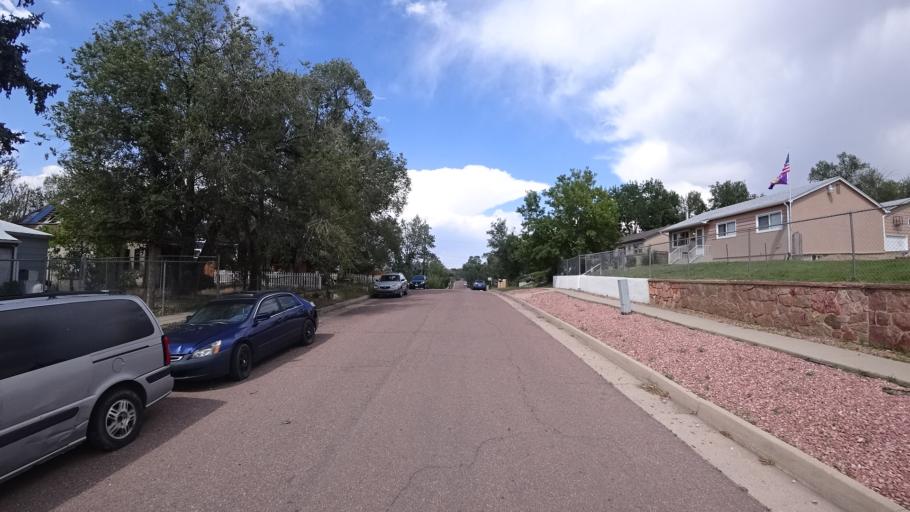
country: US
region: Colorado
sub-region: El Paso County
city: Colorado Springs
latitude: 38.8293
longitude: -104.8106
